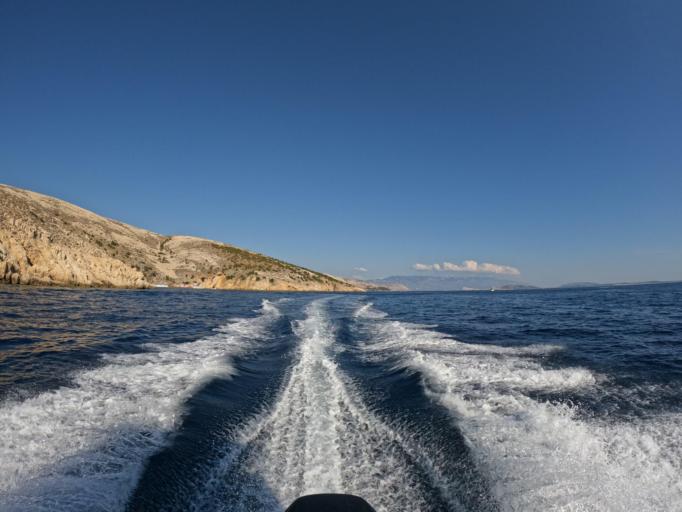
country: HR
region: Primorsko-Goranska
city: Punat
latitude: 44.9664
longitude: 14.6438
